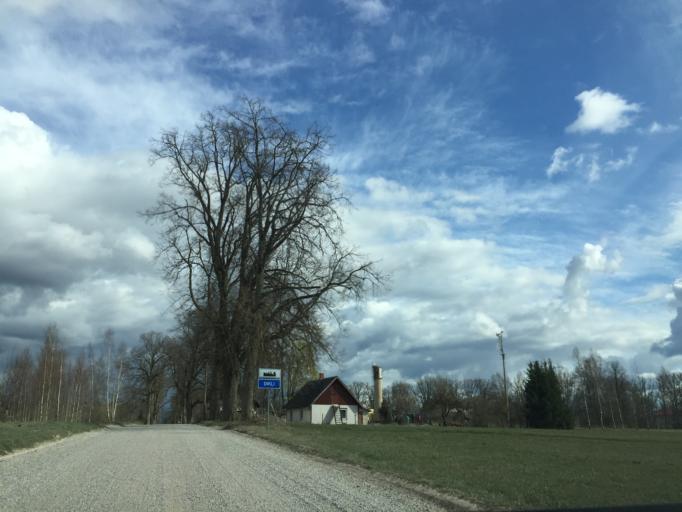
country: LV
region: Burtnieki
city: Matisi
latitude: 57.5999
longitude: 25.0898
